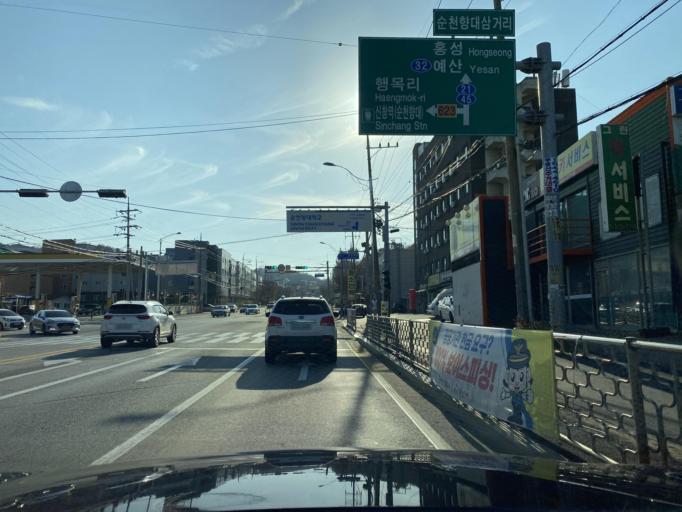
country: KR
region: Chungcheongnam-do
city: Asan
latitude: 36.7752
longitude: 126.9328
